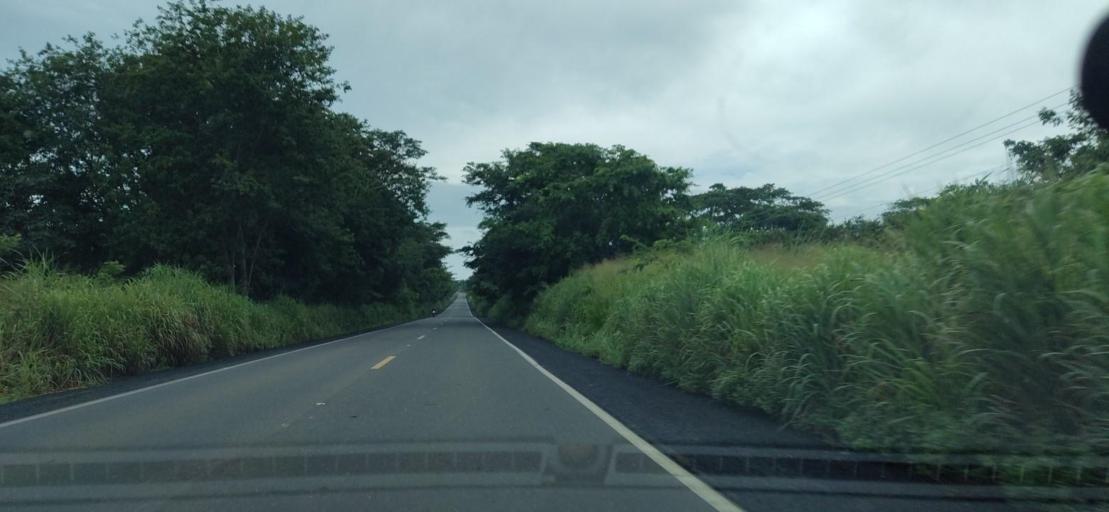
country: BR
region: Piaui
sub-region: Elesbao Veloso
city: Elesbao Veloso
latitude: -6.2004
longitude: -42.1109
